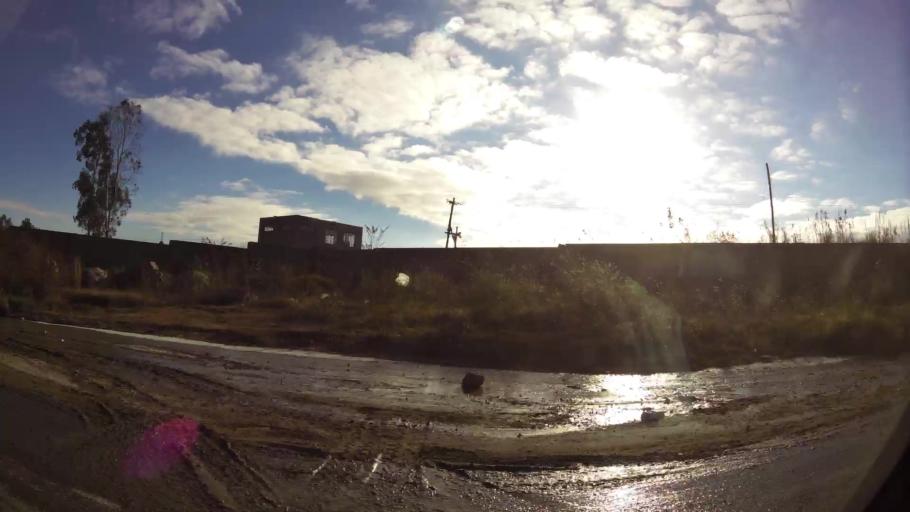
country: ZA
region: Gauteng
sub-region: City of Johannesburg Metropolitan Municipality
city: Modderfontein
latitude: -26.0396
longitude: 28.1683
